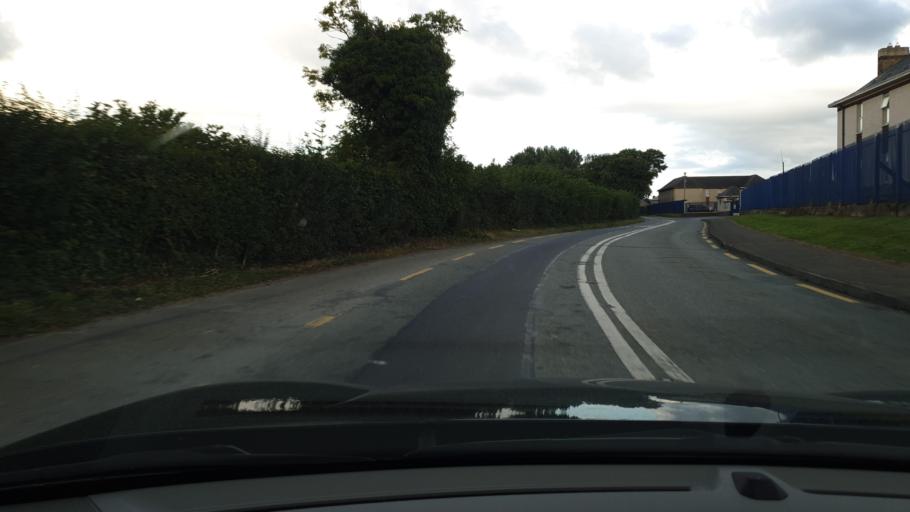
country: IE
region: Leinster
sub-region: South Dublin
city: Saggart
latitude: 53.3100
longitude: -6.4423
